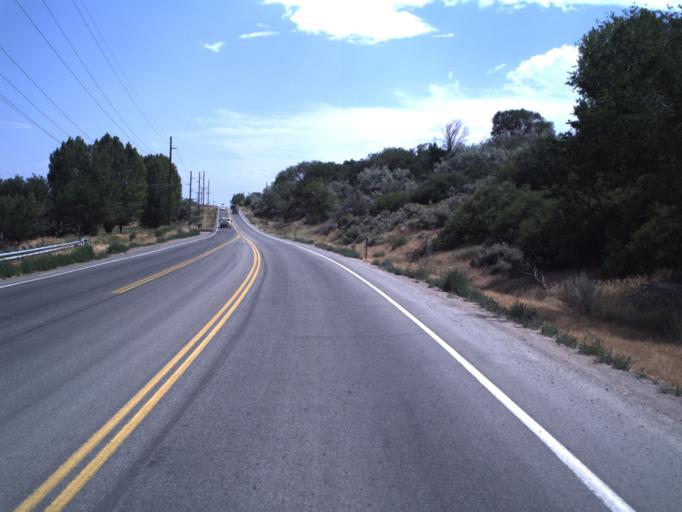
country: US
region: Utah
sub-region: Duchesne County
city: Roosevelt
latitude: 40.3116
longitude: -110.0107
